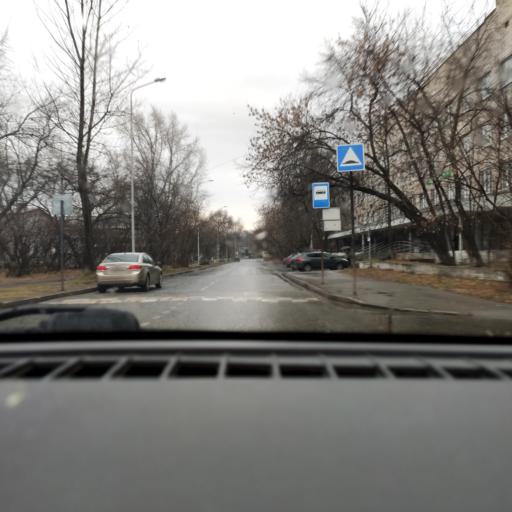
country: RU
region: Perm
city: Kultayevo
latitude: 57.9940
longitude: 55.9351
